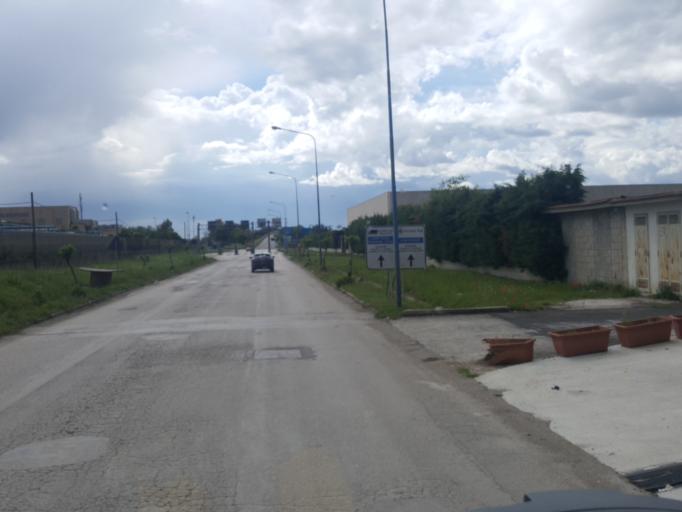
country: IT
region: Campania
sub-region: Provincia di Napoli
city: Pascarola
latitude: 40.9908
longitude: 14.2992
